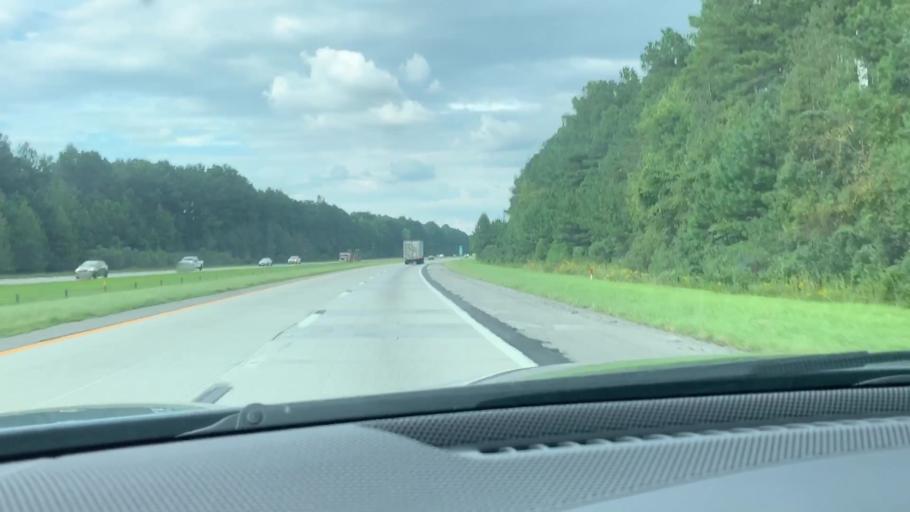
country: US
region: South Carolina
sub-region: Dorchester County
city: Saint George
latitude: 33.3087
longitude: -80.5539
